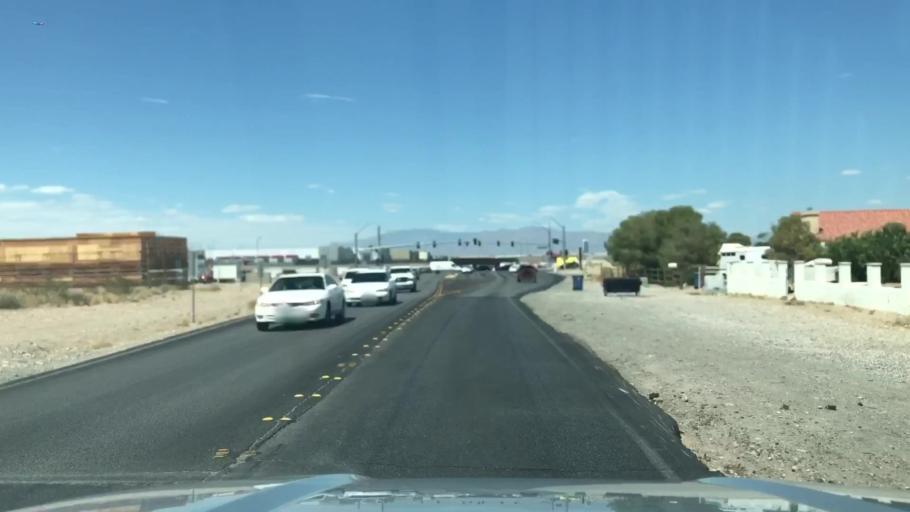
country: US
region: Nevada
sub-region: Clark County
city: Enterprise
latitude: 36.0554
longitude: -115.2078
